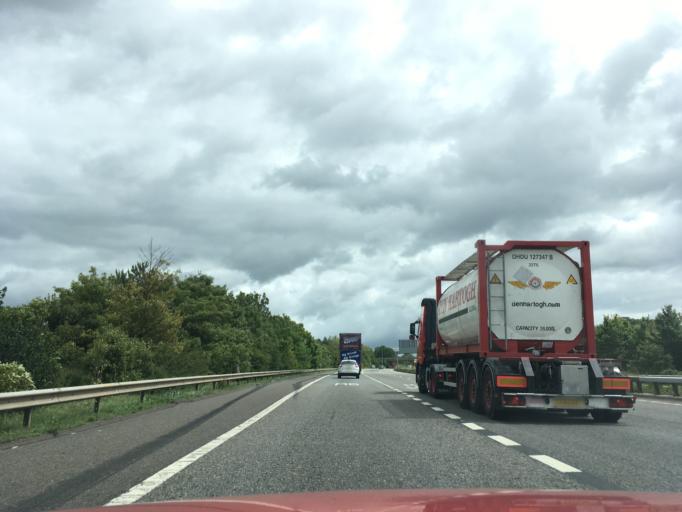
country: GB
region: England
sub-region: South Gloucestershire
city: Almondsbury
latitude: 51.5628
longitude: -2.5641
